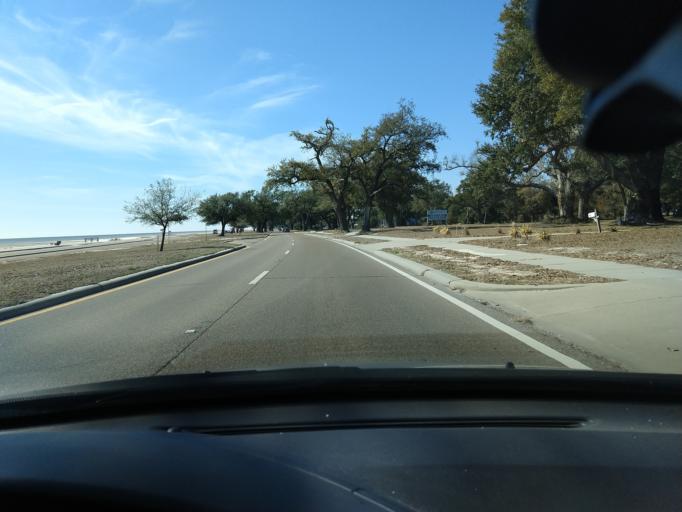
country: US
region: Mississippi
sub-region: Harrison County
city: Long Beach
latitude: 30.3428
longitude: -89.1570
